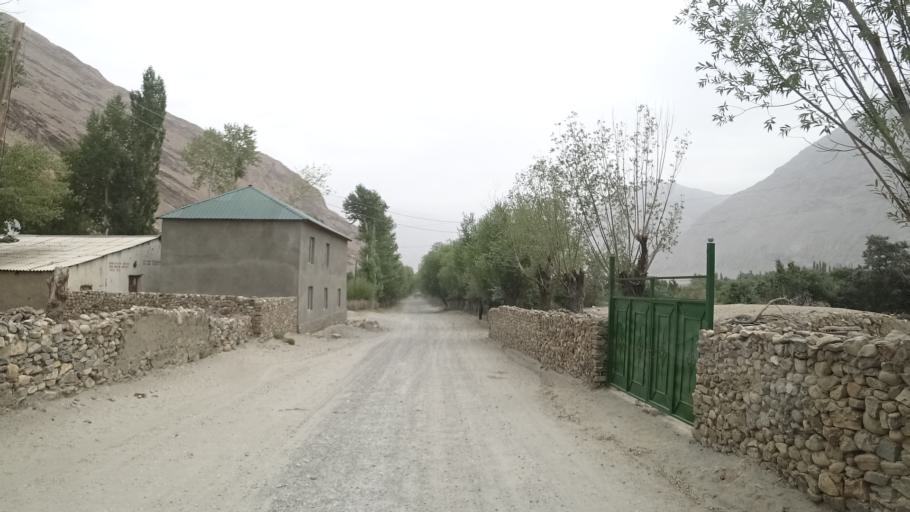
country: AF
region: Badakhshan
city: Khandud
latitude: 37.0218
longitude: 72.5864
